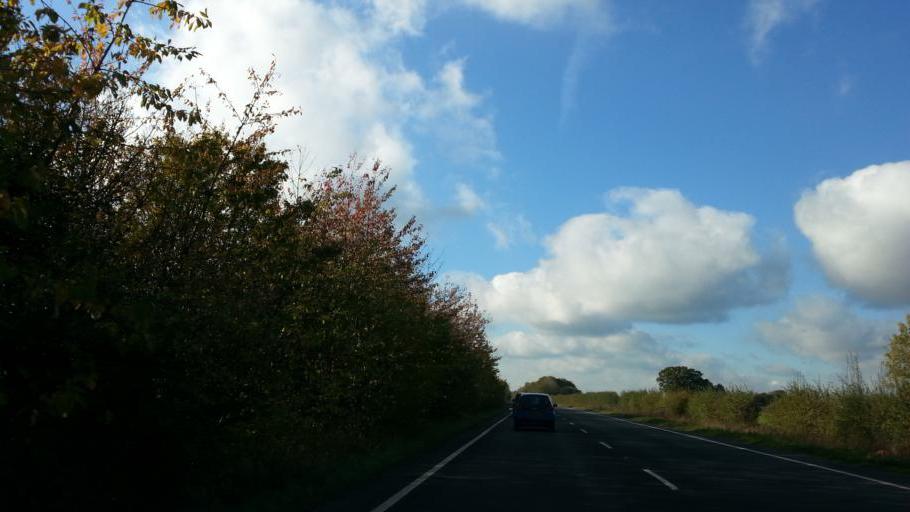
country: GB
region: England
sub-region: Suffolk
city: Beccles
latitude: 52.4844
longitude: 1.5130
